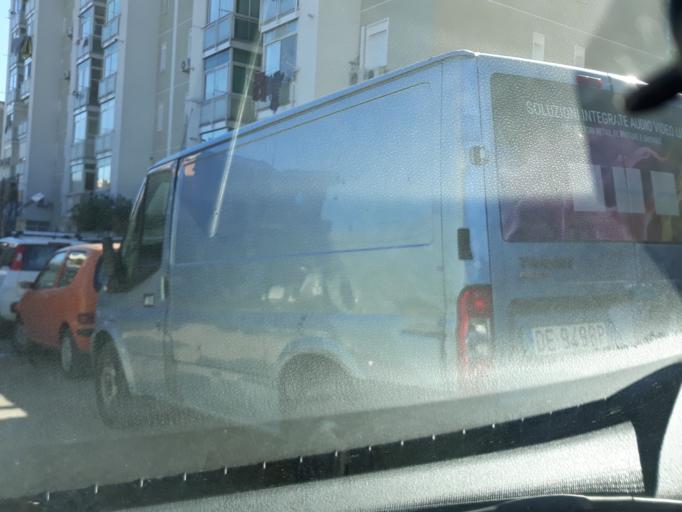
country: IT
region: Sicily
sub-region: Palermo
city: Monreale
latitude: 38.0984
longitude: 13.3163
